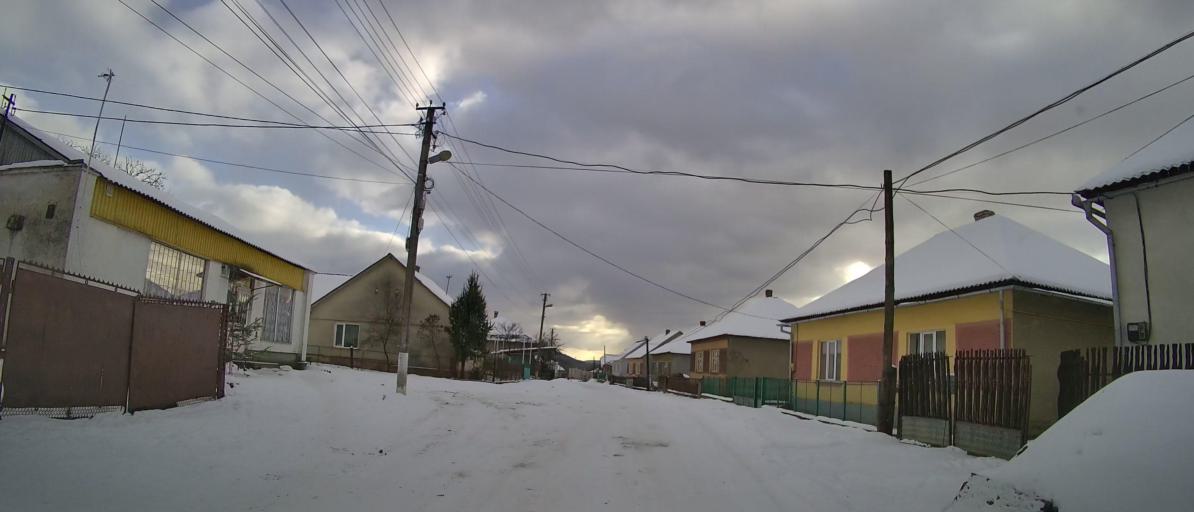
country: UA
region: Zakarpattia
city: Velykyi Bereznyi
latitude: 48.9159
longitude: 22.4641
